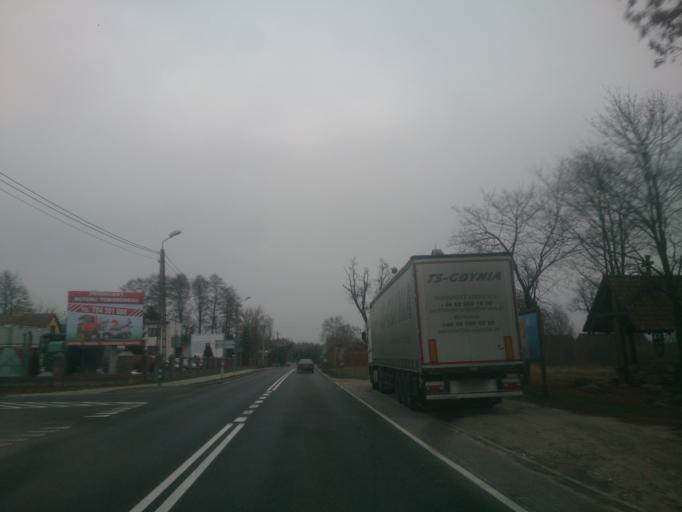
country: PL
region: Warmian-Masurian Voivodeship
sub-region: Powiat nowomiejski
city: Nowe Miasto Lubawskie
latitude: 53.4418
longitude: 19.5967
